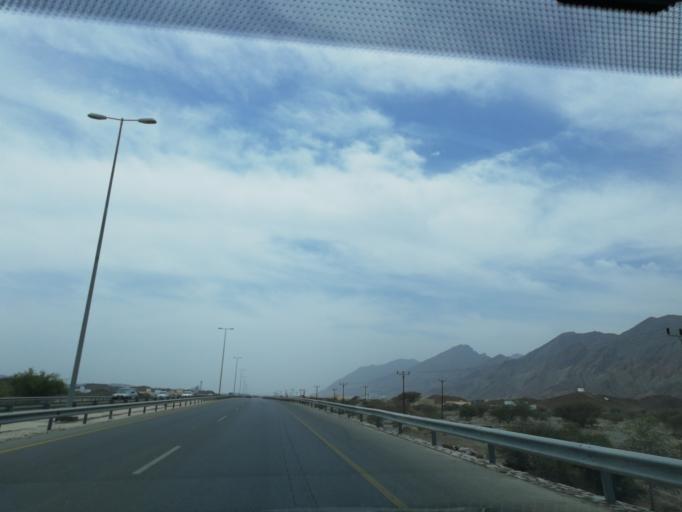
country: OM
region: Muhafazat ad Dakhiliyah
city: Izki
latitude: 23.0390
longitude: 57.8012
